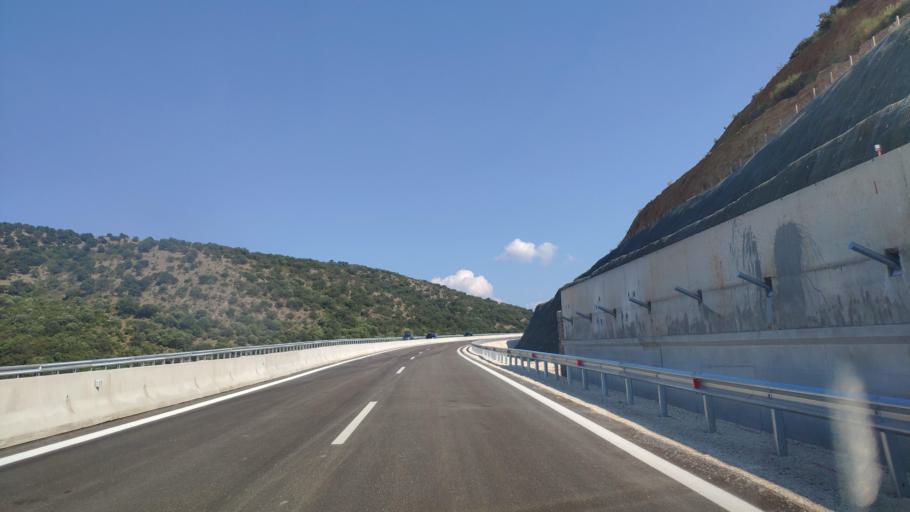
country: GR
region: West Greece
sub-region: Nomos Aitolias kai Akarnanias
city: Amfilochia
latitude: 38.8629
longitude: 21.0785
